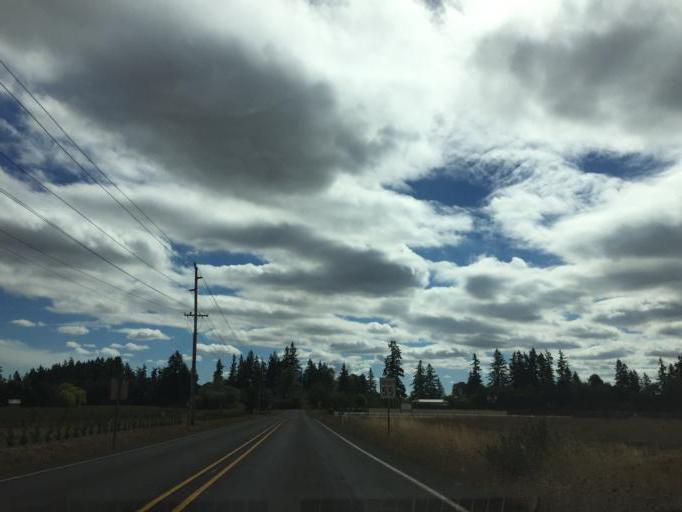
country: US
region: Oregon
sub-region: Marion County
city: Woodburn
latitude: 45.1335
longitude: -122.8335
